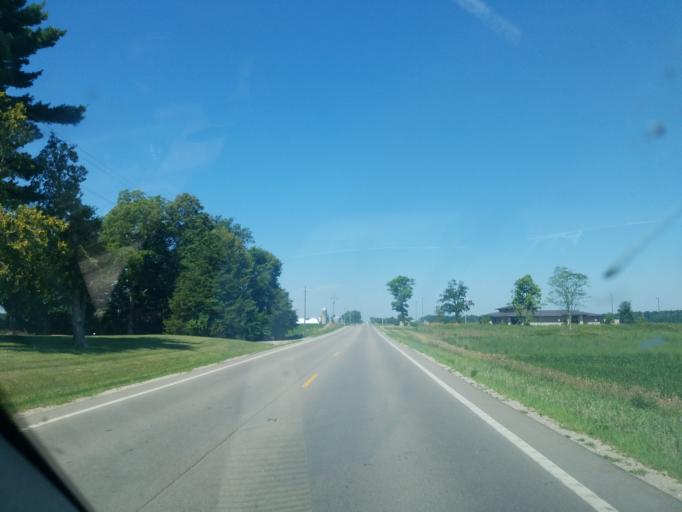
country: US
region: Ohio
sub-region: Shelby County
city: Botkins
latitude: 40.4388
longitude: -84.1392
